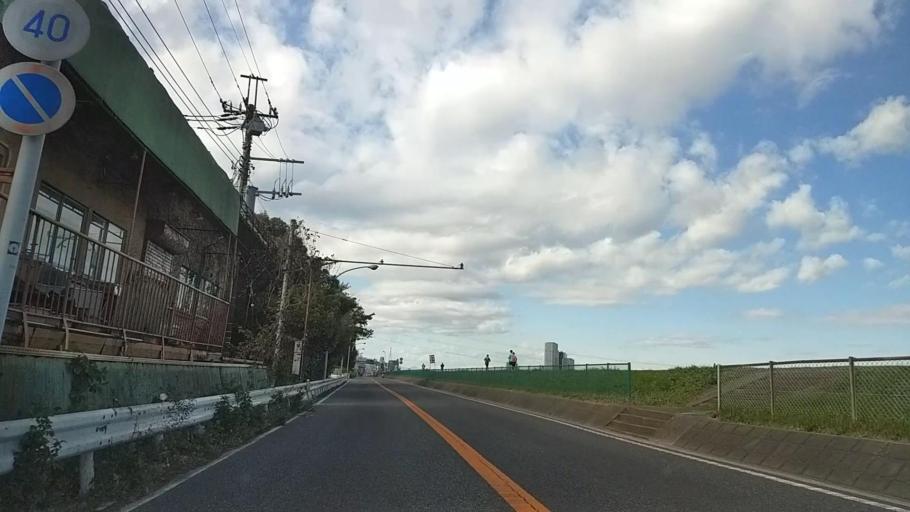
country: JP
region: Kanagawa
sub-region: Kawasaki-shi
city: Kawasaki
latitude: 35.5917
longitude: 139.6492
